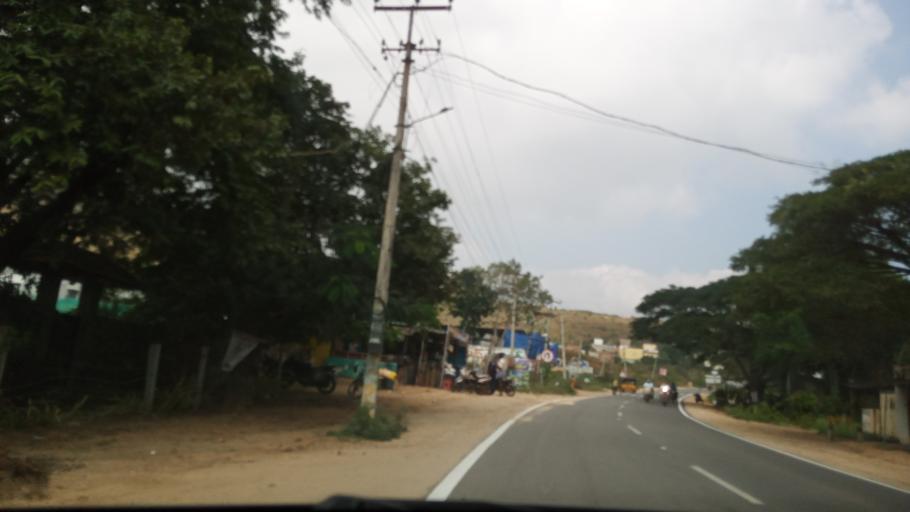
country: IN
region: Andhra Pradesh
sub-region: Chittoor
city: Madanapalle
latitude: 13.5823
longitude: 78.5211
